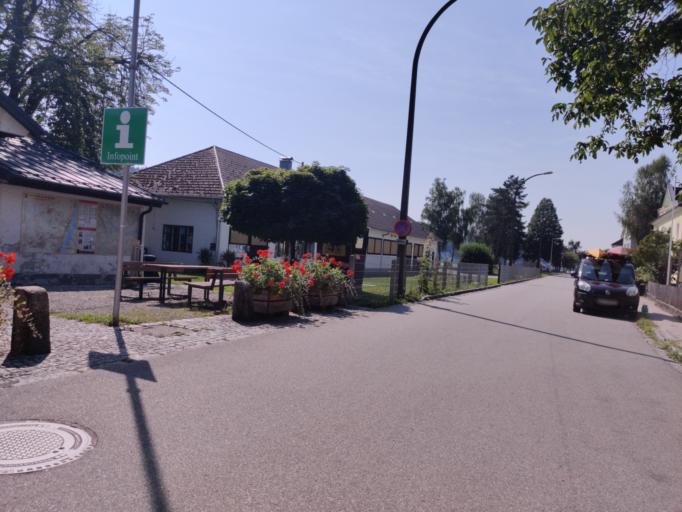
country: AT
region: Upper Austria
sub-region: Politischer Bezirk Urfahr-Umgebung
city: Feldkirchen an der Donau
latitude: 48.3741
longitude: 14.0282
